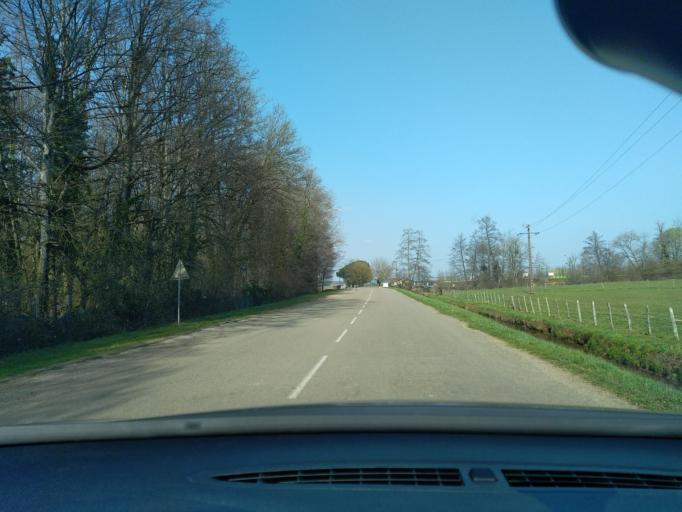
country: FR
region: Franche-Comte
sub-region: Departement du Jura
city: Mont-sous-Vaudrey
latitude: 46.9833
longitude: 5.6054
